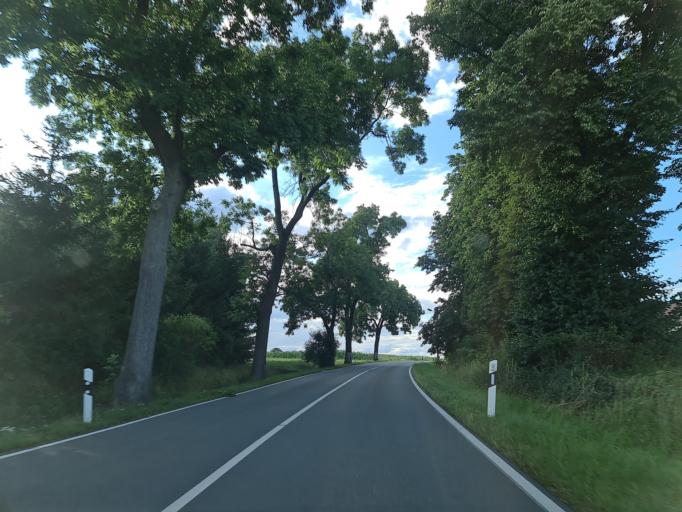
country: DE
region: Saxony
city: Pausa
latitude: 50.5659
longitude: 12.0027
